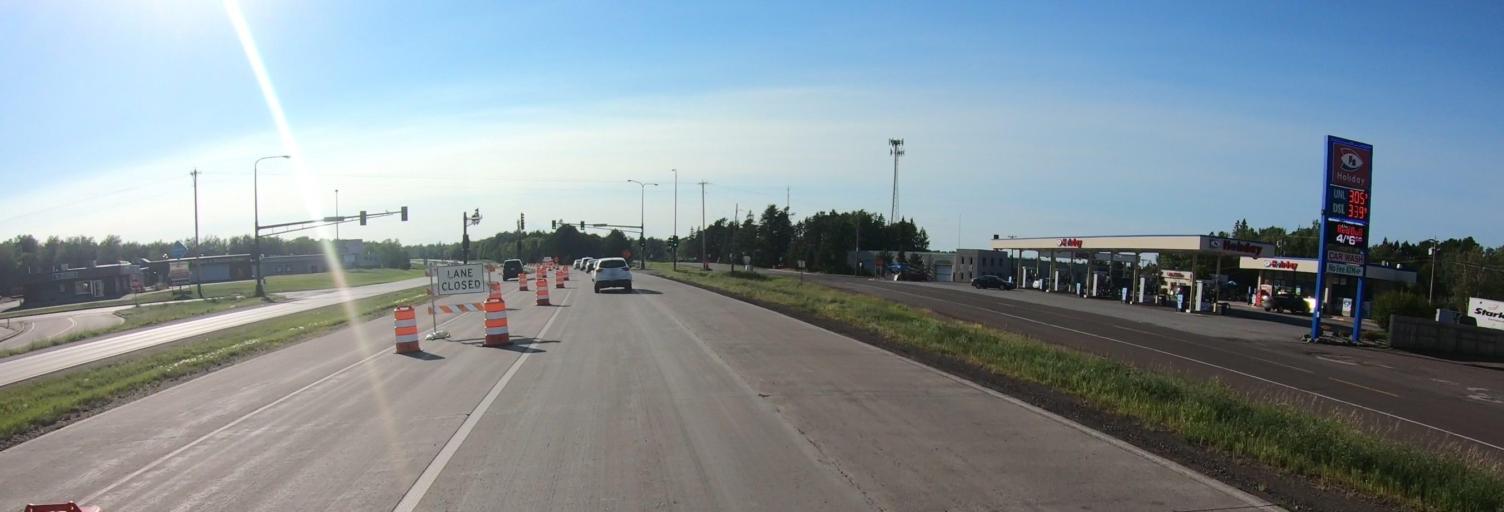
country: US
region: Minnesota
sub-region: Saint Louis County
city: Hermantown
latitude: 46.8502
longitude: -92.2820
